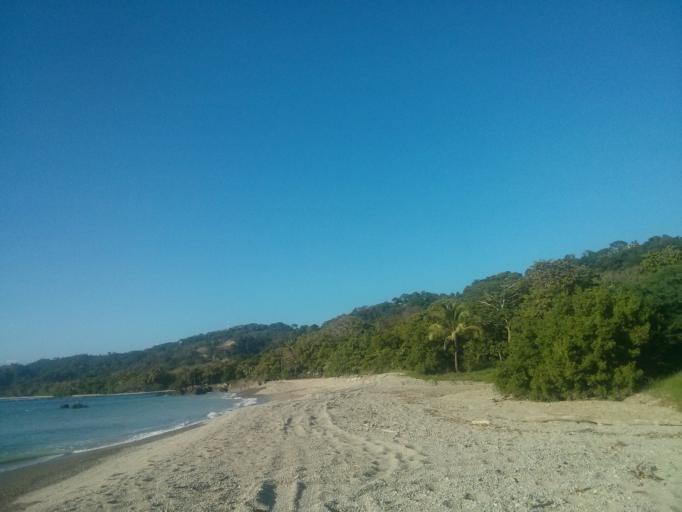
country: CR
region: Puntarenas
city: Paquera
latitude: 9.6119
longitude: -85.1442
